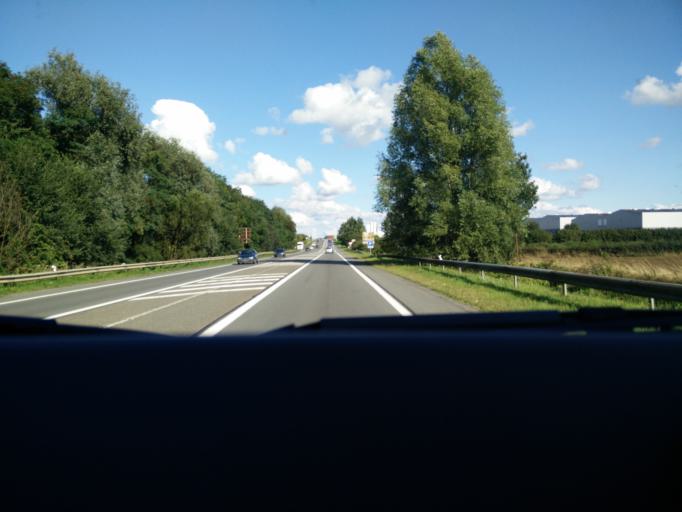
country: FR
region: Nord-Pas-de-Calais
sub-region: Departement du Nord
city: Feignies
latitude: 50.2817
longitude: 3.8960
